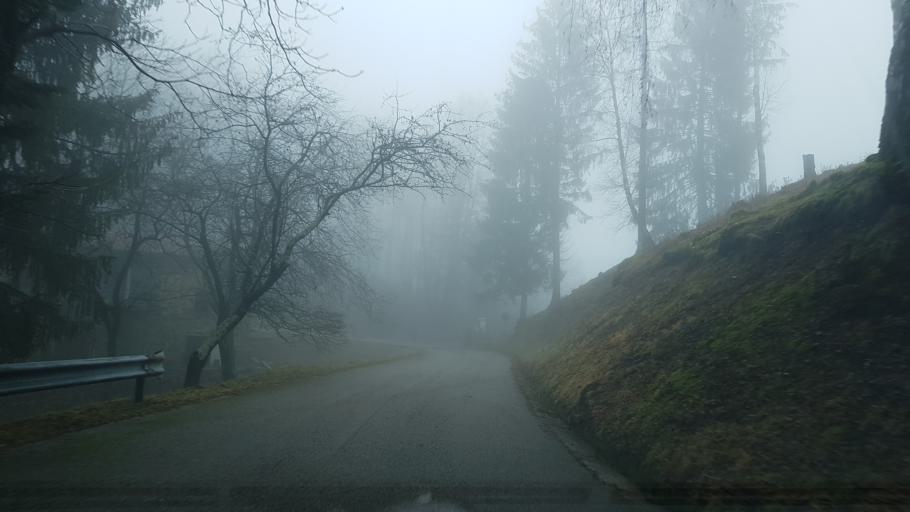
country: IT
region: Friuli Venezia Giulia
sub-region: Provincia di Udine
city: Stregna
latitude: 46.1218
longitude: 13.5990
